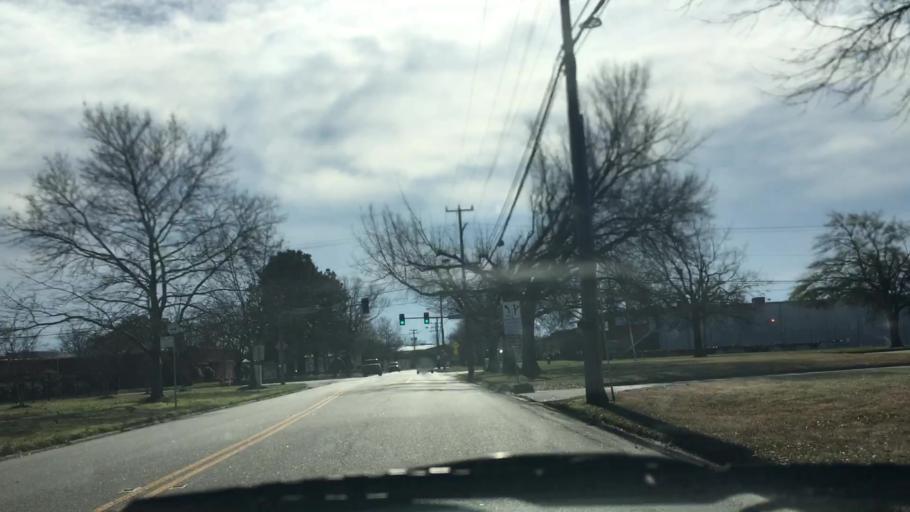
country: US
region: Virginia
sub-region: City of Norfolk
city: Norfolk
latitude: 36.8624
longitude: -76.2344
